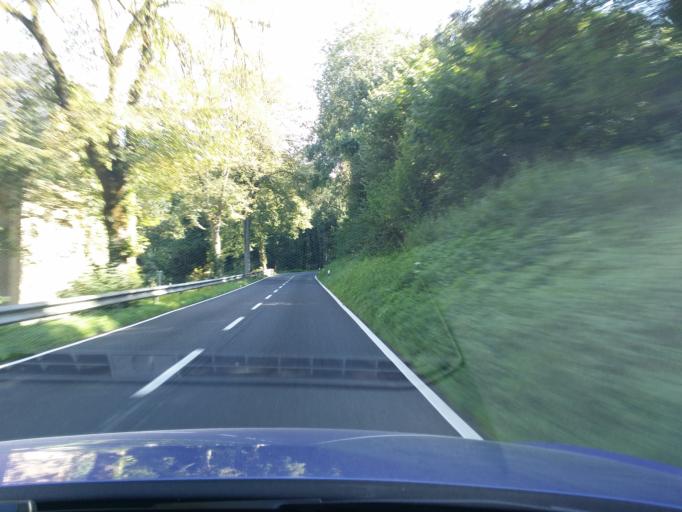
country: LU
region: Luxembourg
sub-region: Canton de Luxembourg
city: Bertrange
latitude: 49.6325
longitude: 6.0461
